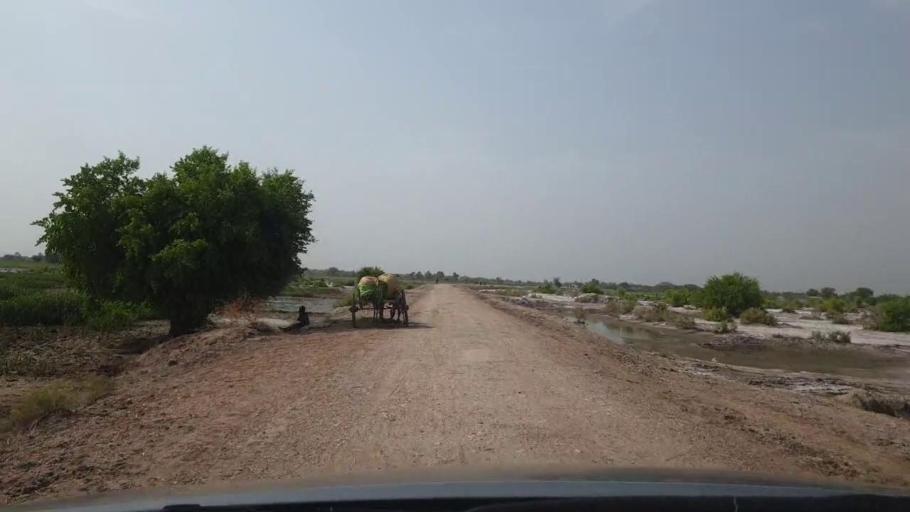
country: PK
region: Sindh
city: Rohri
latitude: 27.6705
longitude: 69.0134
